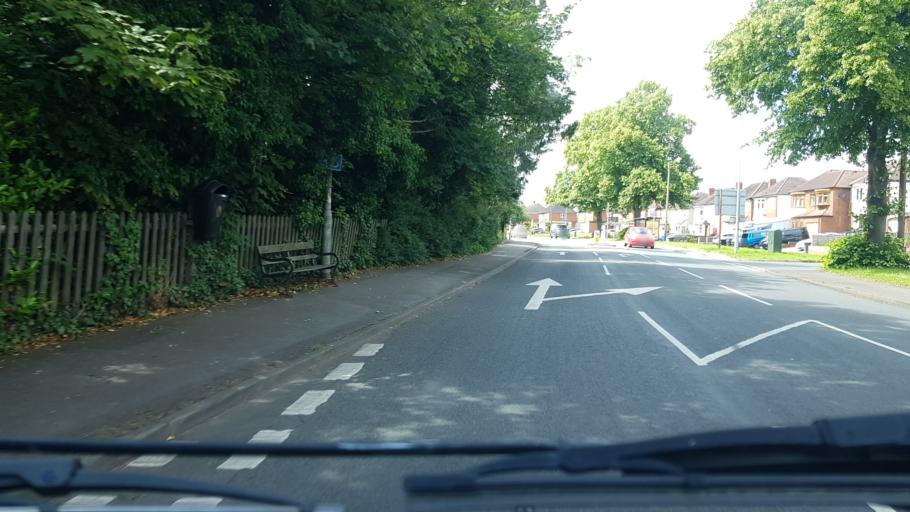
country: GB
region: England
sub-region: Worcestershire
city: Stourport-on-Severn
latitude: 52.3439
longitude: -2.2784
